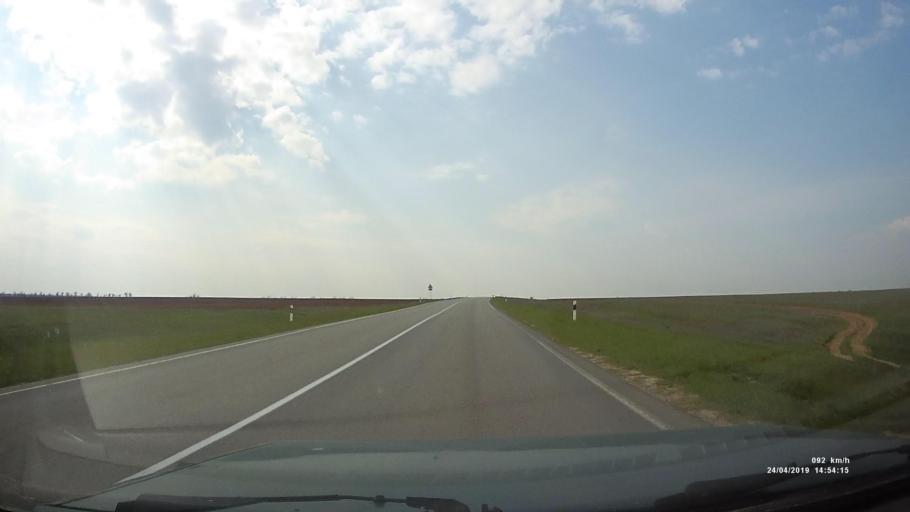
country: RU
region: Rostov
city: Remontnoye
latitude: 46.5332
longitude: 43.6422
